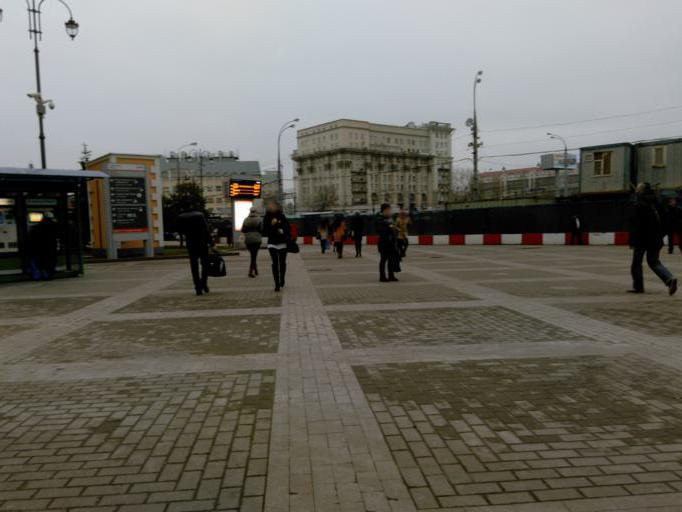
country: RU
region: Moscow
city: Mar'ina Roshcha
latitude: 55.7942
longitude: 37.5873
